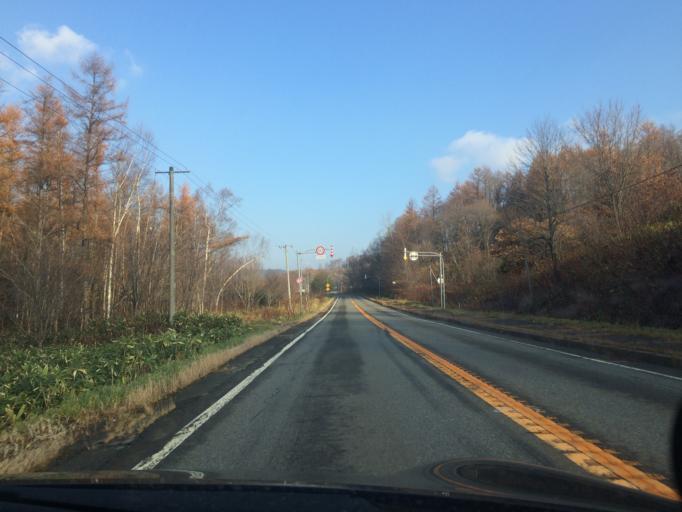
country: JP
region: Hokkaido
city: Shimo-furano
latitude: 42.8939
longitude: 142.4304
